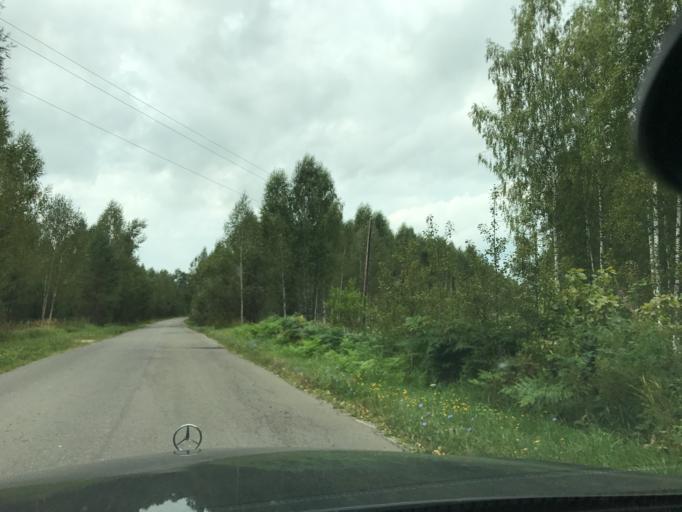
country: RU
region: Vladimir
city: Galitsy
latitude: 55.9959
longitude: 42.8236
